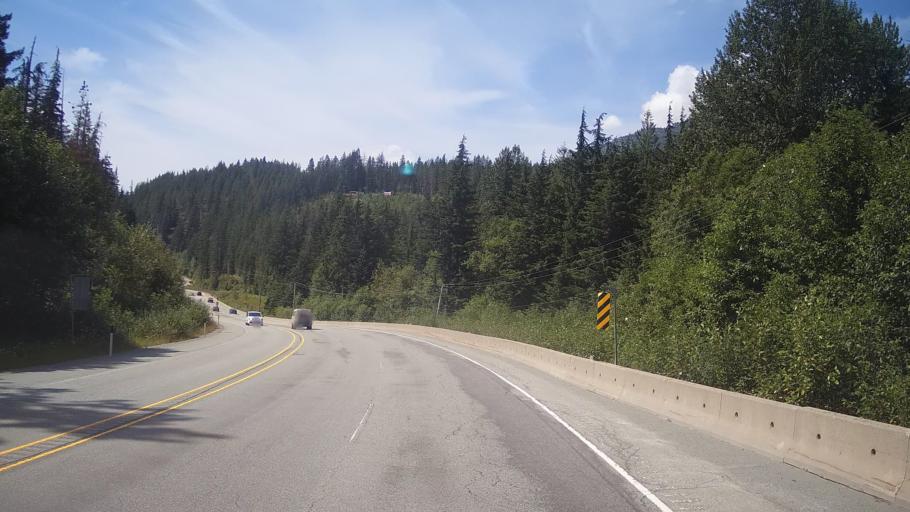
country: CA
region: British Columbia
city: Whistler
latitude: 50.0508
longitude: -123.1245
